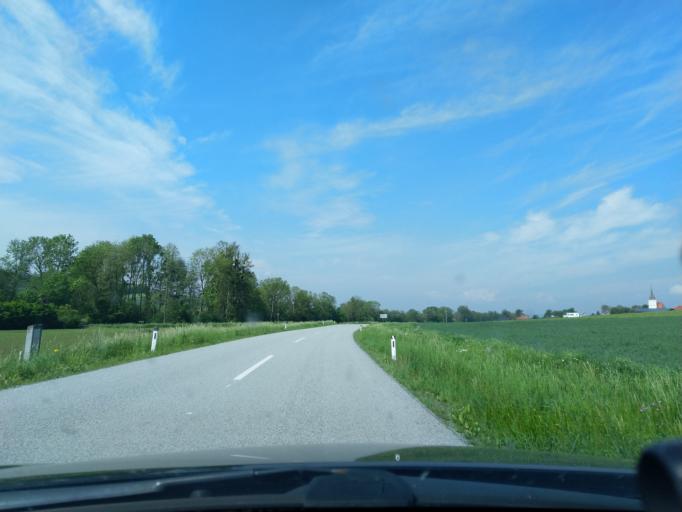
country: DE
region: Bavaria
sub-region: Lower Bavaria
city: Bad Fussing
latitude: 48.3007
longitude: 13.3743
